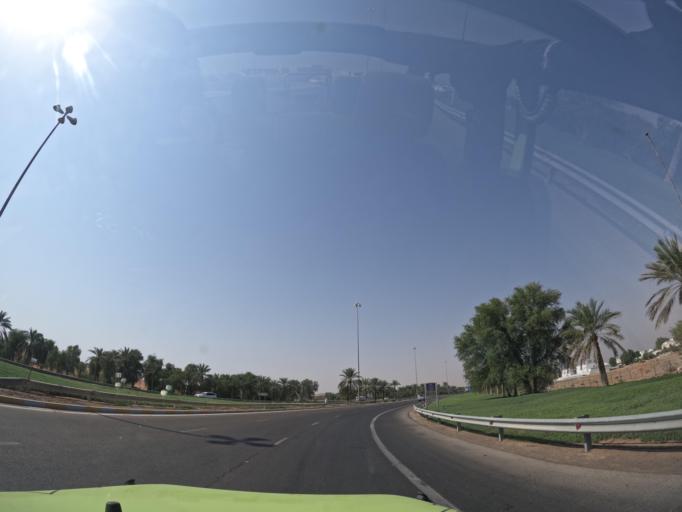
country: AE
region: Abu Dhabi
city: Al Ain
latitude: 24.2026
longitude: 55.5933
